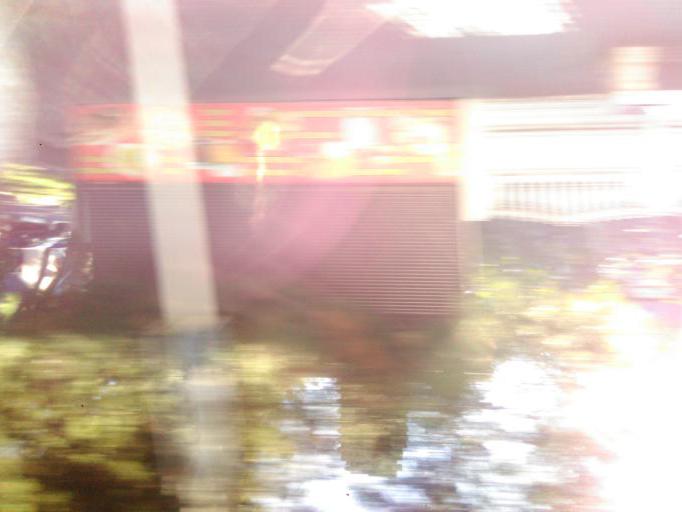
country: RU
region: Krasnodarskiy
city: Gelendzhik
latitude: 44.5531
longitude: 38.0702
